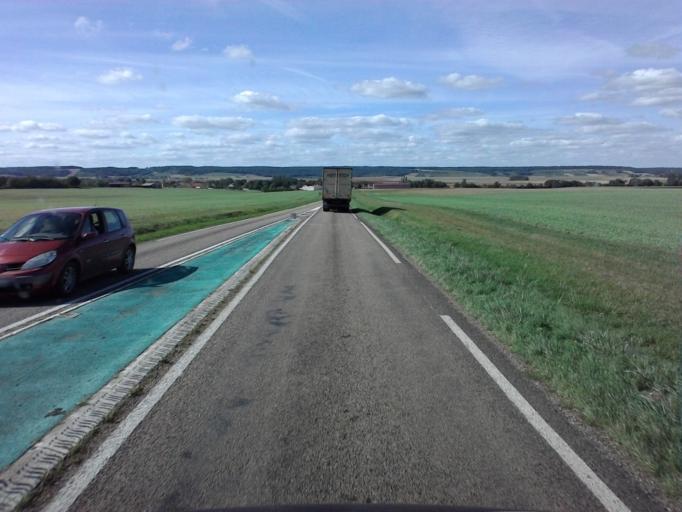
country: FR
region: Bourgogne
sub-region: Departement de la Cote-d'Or
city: Chatillon-sur-Seine
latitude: 47.9107
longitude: 4.6788
